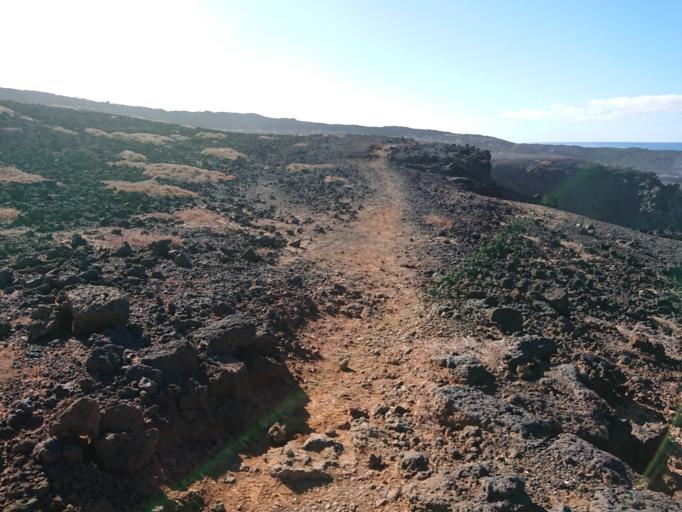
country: ES
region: Canary Islands
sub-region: Provincia de Las Palmas
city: Tinajo
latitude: 29.0812
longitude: -13.7264
